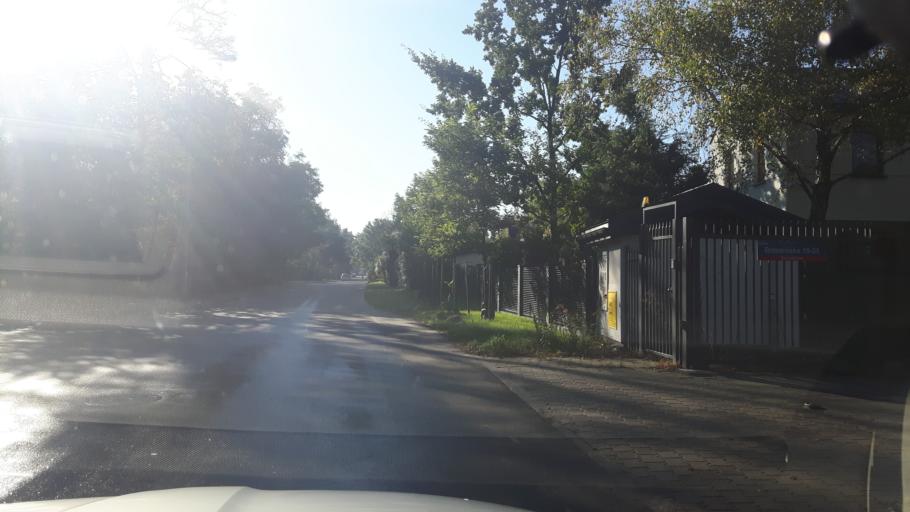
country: PL
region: Masovian Voivodeship
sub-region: Warszawa
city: Bialoleka
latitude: 52.3568
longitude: 20.9776
